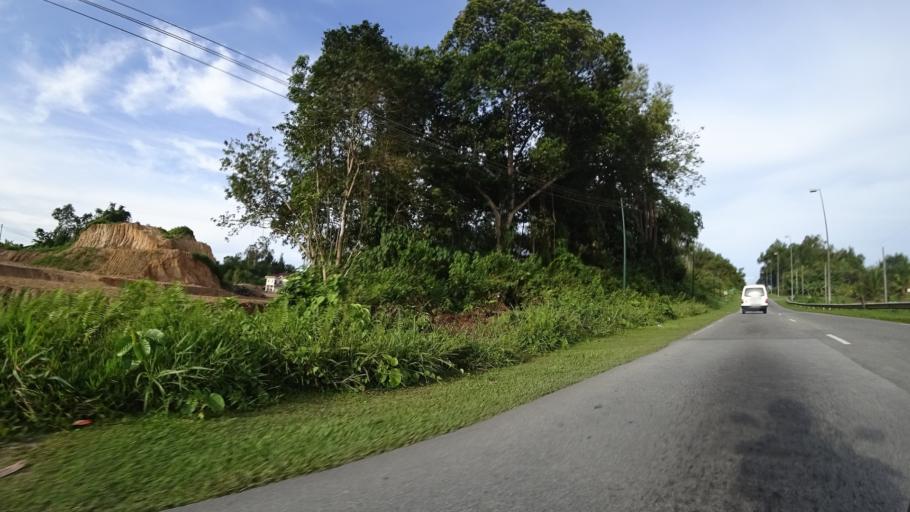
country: BN
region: Brunei and Muara
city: Bandar Seri Begawan
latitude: 4.8696
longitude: 114.8134
